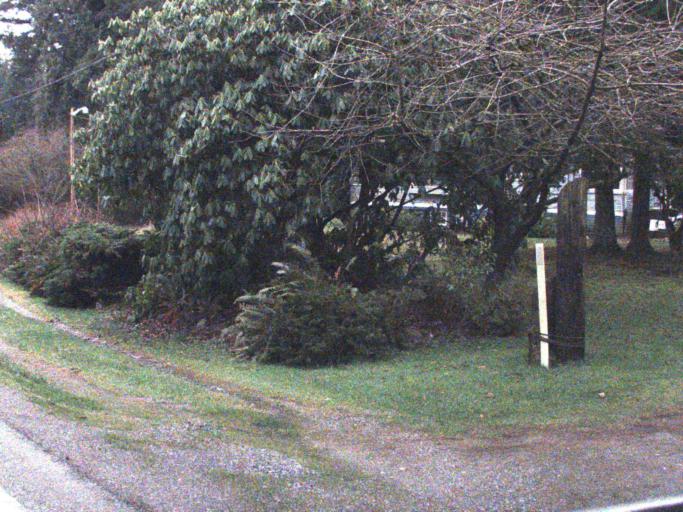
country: US
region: Washington
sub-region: Snohomish County
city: Smokey Point
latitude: 48.1563
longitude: -122.2443
